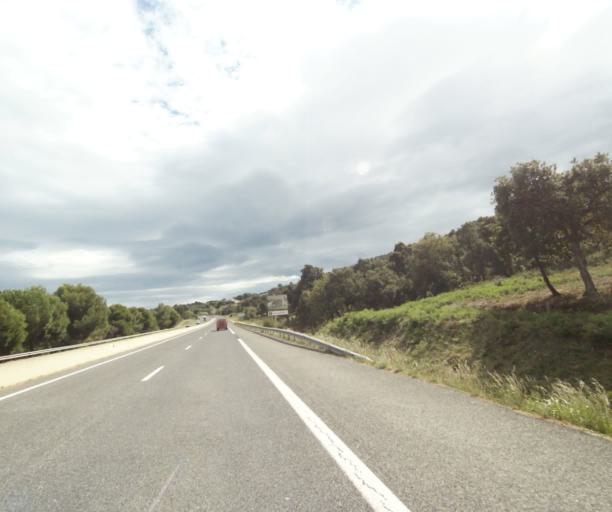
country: FR
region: Languedoc-Roussillon
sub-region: Departement des Pyrenees-Orientales
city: Argelers
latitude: 42.5335
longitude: 3.0458
